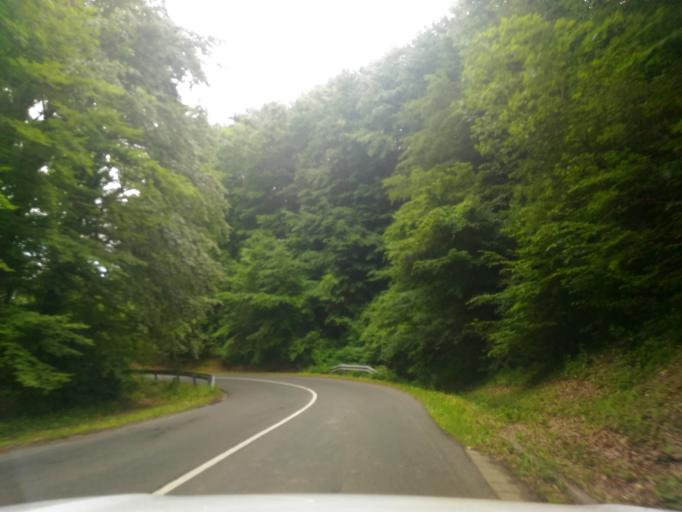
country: HU
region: Baranya
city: Komlo
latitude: 46.1811
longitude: 18.2138
